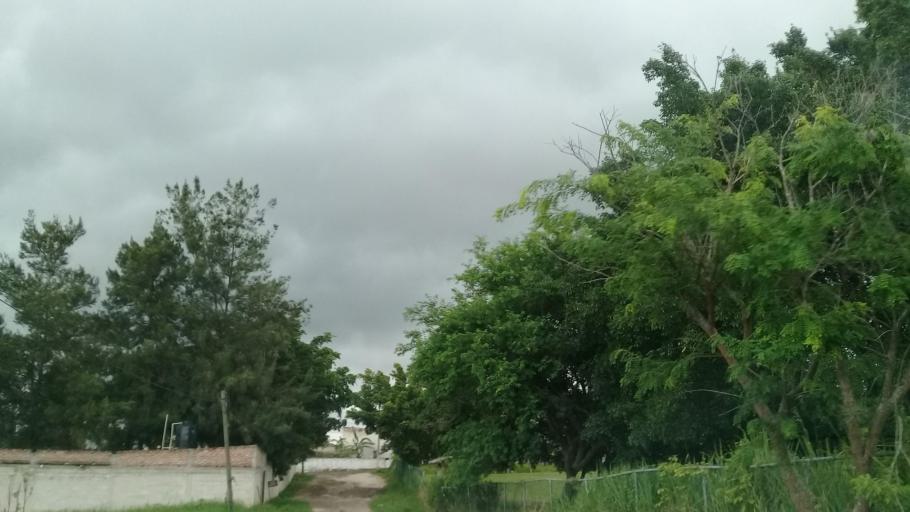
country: MX
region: Veracruz
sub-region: Emiliano Zapata
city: Dos Rios
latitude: 19.4867
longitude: -96.7994
